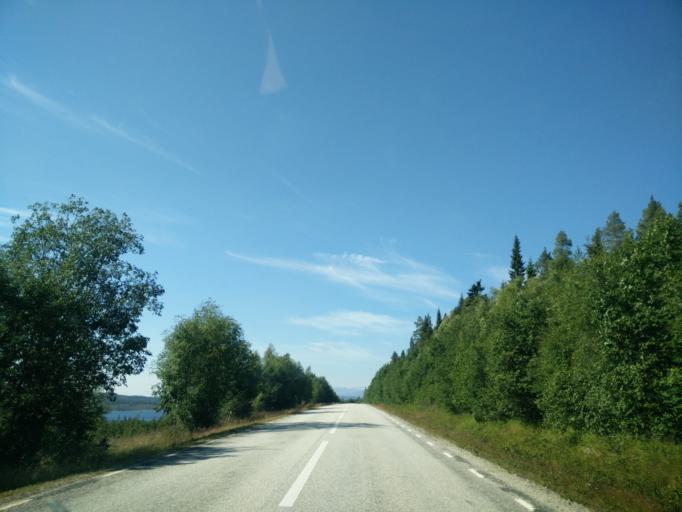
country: SE
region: Jaemtland
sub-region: Are Kommun
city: Jarpen
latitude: 62.8021
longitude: 13.5556
